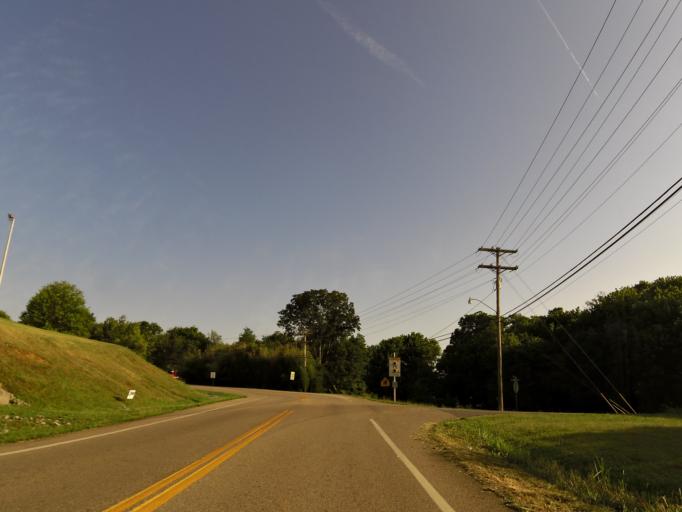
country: US
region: Tennessee
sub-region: Blount County
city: Louisville
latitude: 35.7639
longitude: -84.1319
